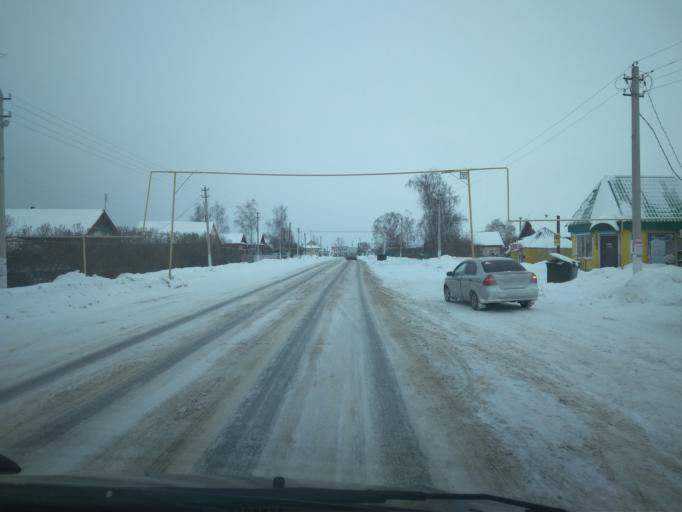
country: RU
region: Mordoviya
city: Kemlya
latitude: 54.6886
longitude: 45.2740
